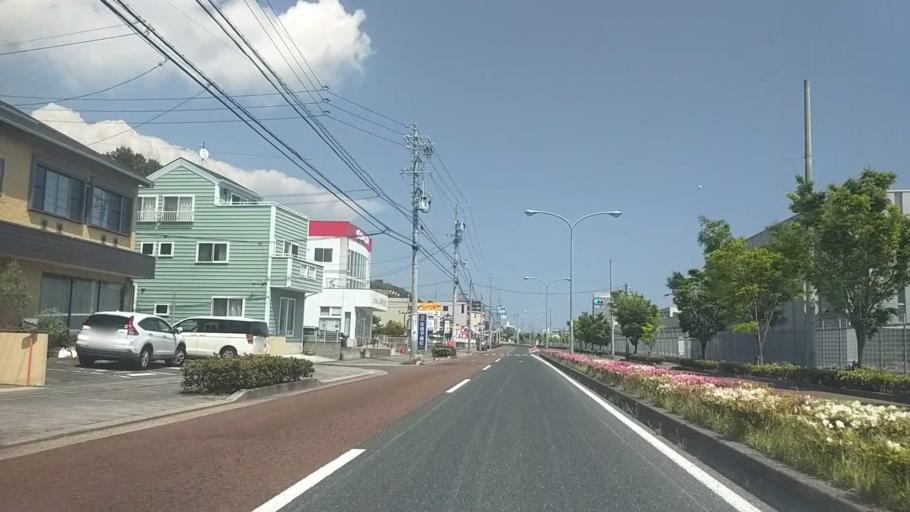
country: JP
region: Shizuoka
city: Hamamatsu
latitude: 34.6998
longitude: 137.7107
